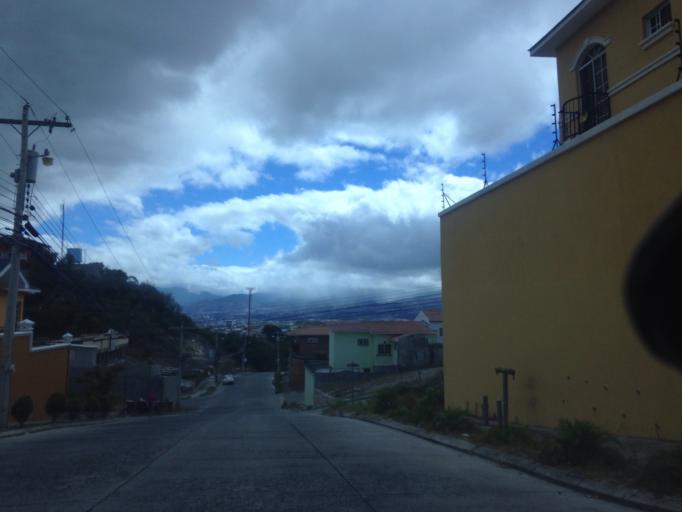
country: HN
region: Francisco Morazan
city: Yaguacire
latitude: 14.0526
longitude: -87.2404
